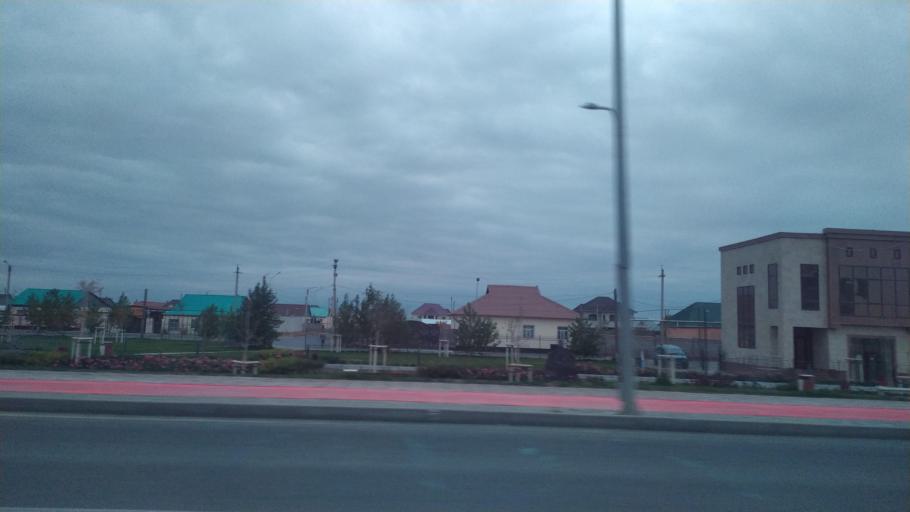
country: KZ
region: Ongtustik Qazaqstan
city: Turkestan
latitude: 43.2779
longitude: 68.3282
